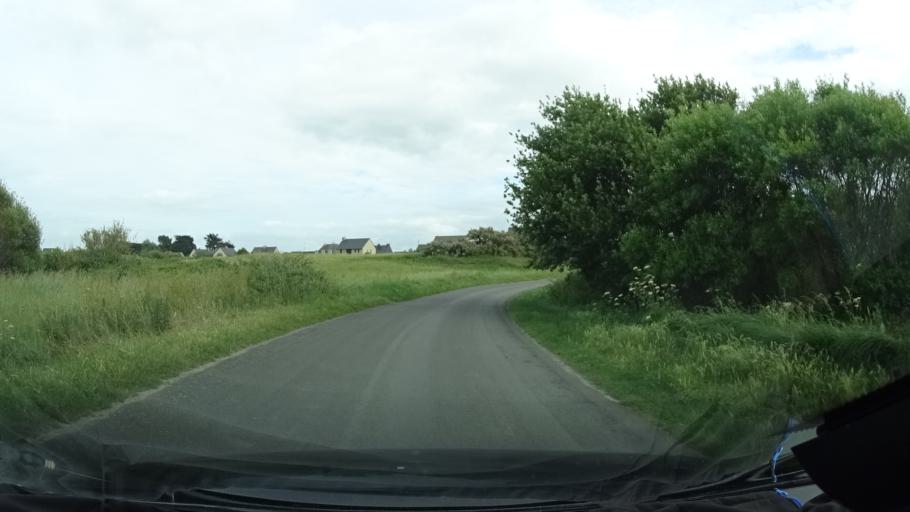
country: FR
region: Brittany
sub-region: Departement d'Ille-et-Vilaine
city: Saint-Malo
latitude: 48.6802
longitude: -1.9848
